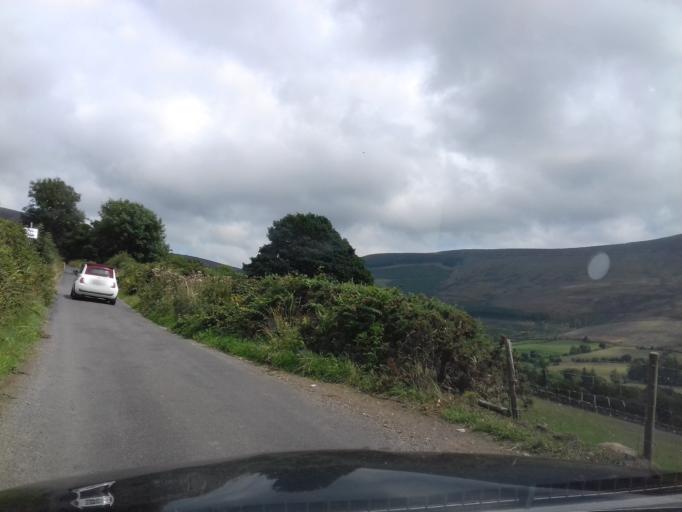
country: IE
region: Leinster
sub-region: Kilkenny
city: Graiguenamanagh
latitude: 52.6241
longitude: -6.8261
